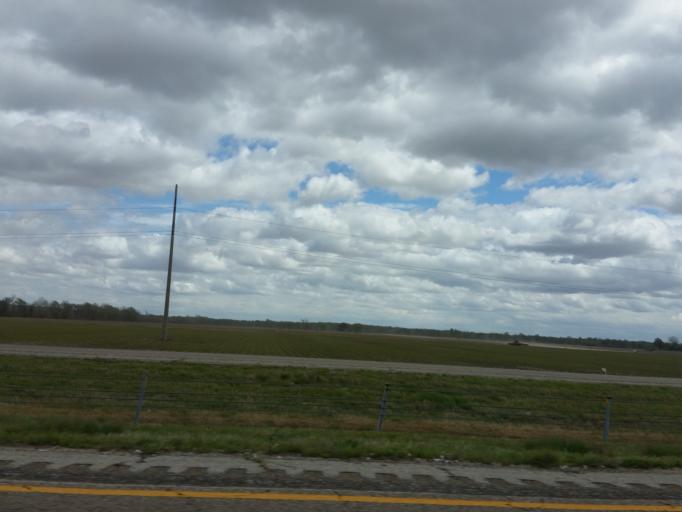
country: US
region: Arkansas
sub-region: Poinsett County
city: Trumann
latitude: 35.5996
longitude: -90.4968
